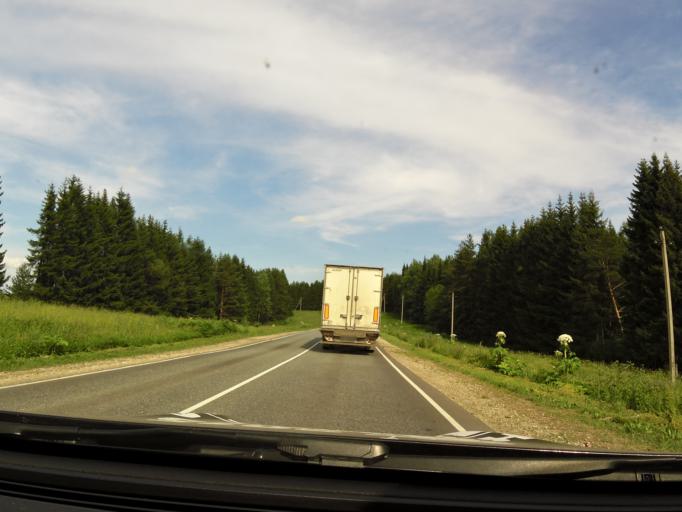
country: RU
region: Kirov
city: Slobodskoy
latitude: 58.7519
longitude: 50.3183
